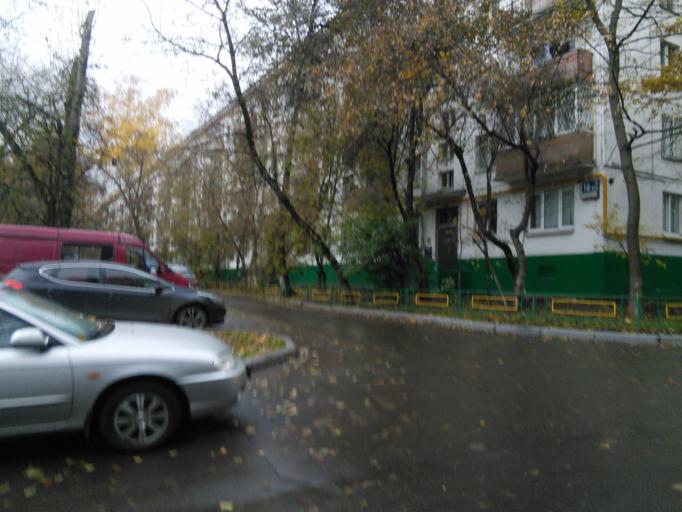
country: RU
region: Moscow
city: Tsaritsyno
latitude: 55.6362
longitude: 37.6551
